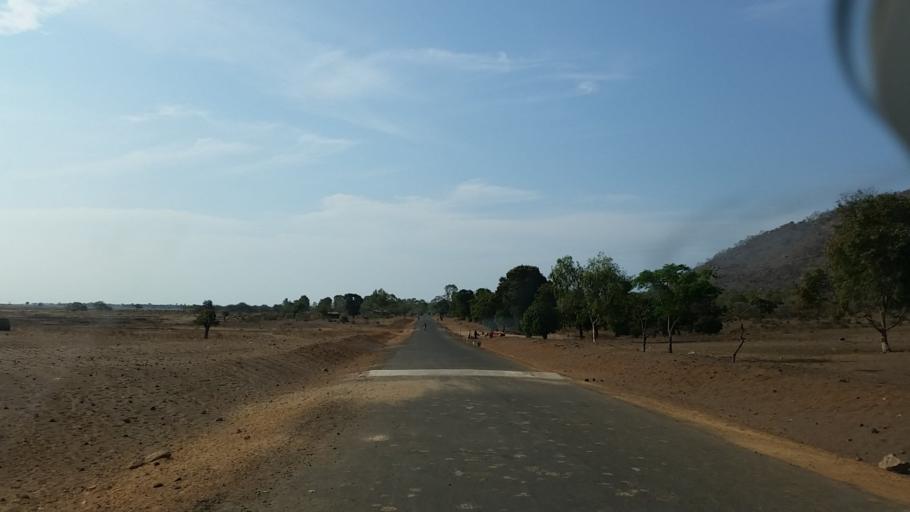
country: MW
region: Central Region
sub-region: Salima District
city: Salima
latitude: -13.6867
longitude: 34.5876
